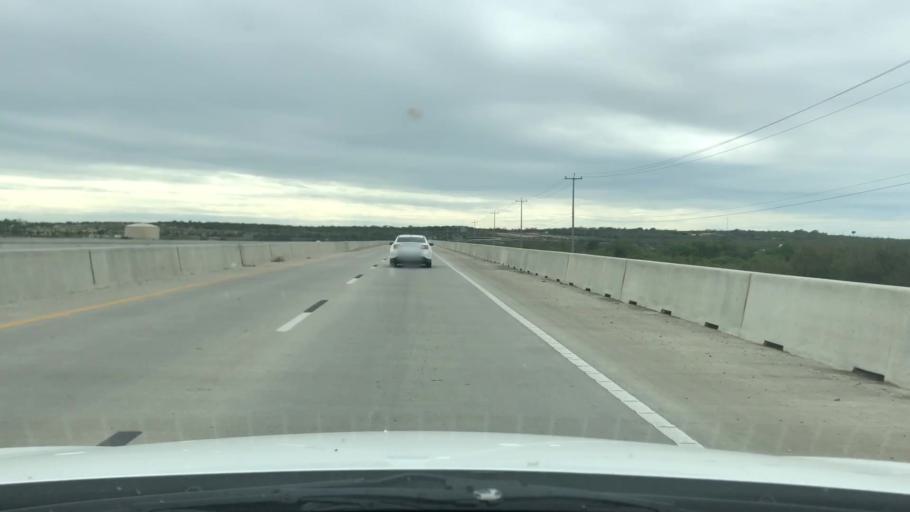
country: US
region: Texas
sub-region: Bexar County
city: Converse
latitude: 29.4852
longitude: -98.2944
